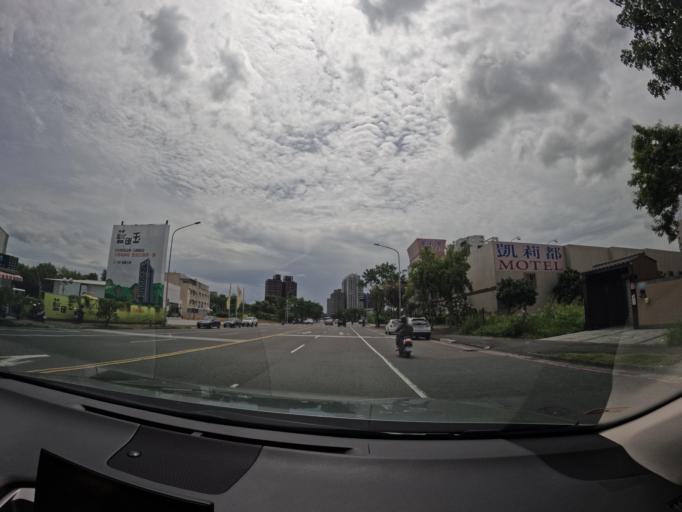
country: TW
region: Kaohsiung
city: Kaohsiung
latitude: 22.7276
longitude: 120.2895
